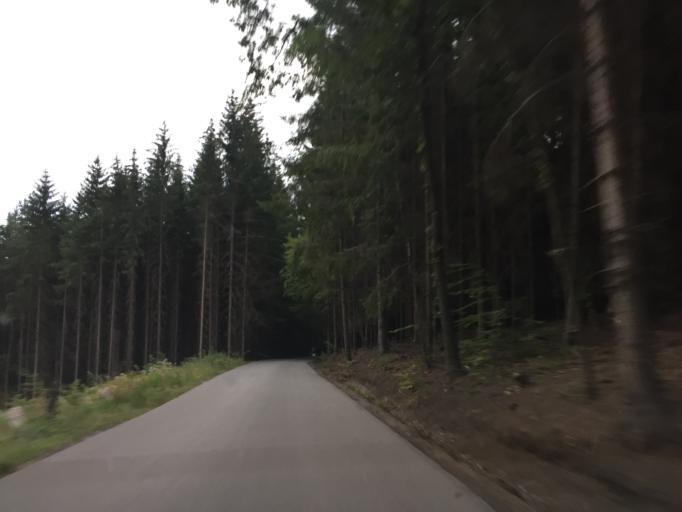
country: CZ
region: Liberecky
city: Mala Skala
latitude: 50.6375
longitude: 15.2045
